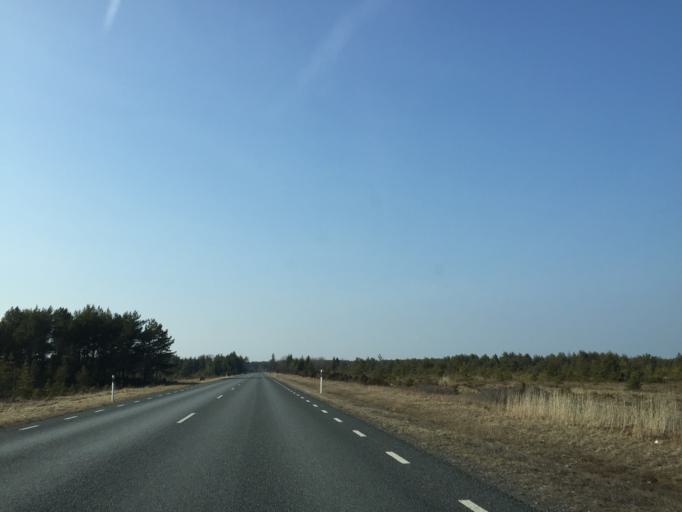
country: EE
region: Saare
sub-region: Orissaare vald
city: Orissaare
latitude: 58.5874
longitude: 23.3428
